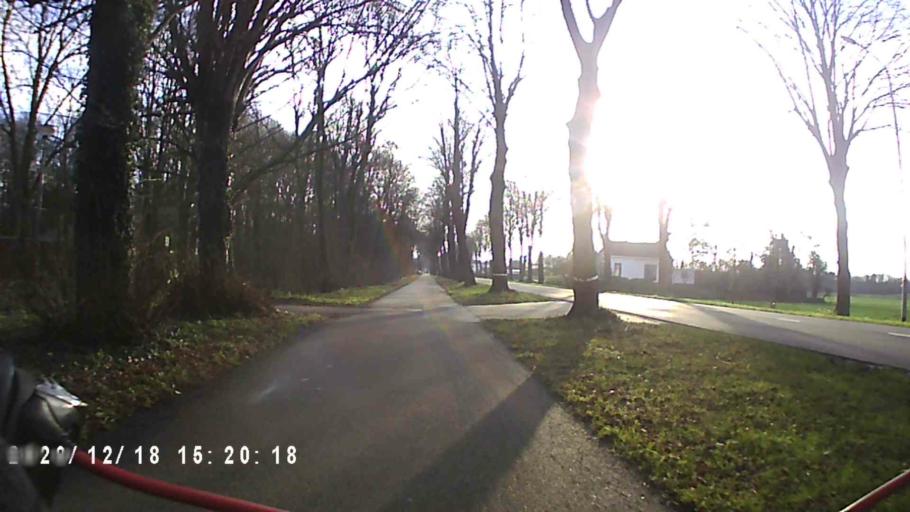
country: NL
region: Groningen
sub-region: Gemeente Hoogezand-Sappemeer
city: Hoogezand
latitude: 53.1555
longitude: 6.7232
